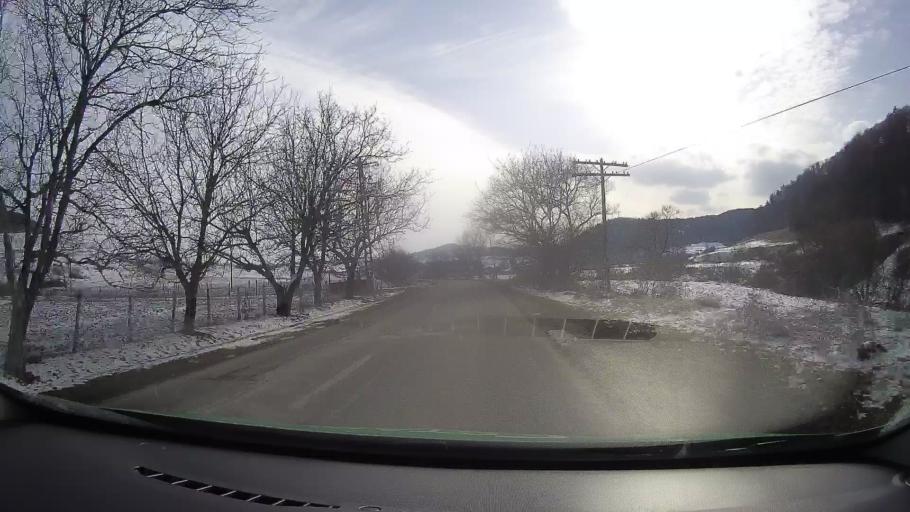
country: RO
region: Mures
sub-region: Comuna Apold
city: Apold
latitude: 46.1371
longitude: 24.8197
